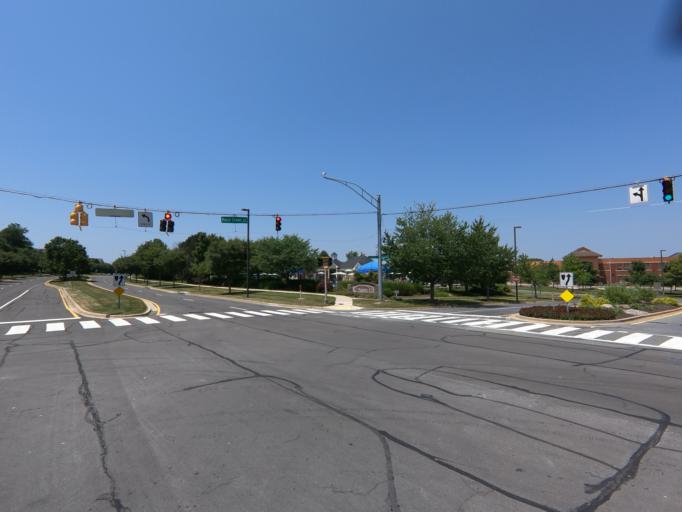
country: US
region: Maryland
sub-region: Montgomery County
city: Germantown
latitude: 39.2039
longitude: -77.2599
